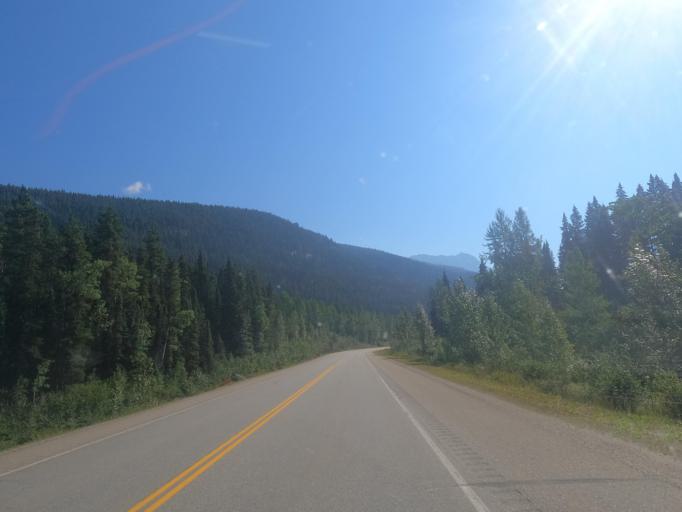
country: CA
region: Alberta
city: Jasper Park Lodge
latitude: 52.8927
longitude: -118.7380
